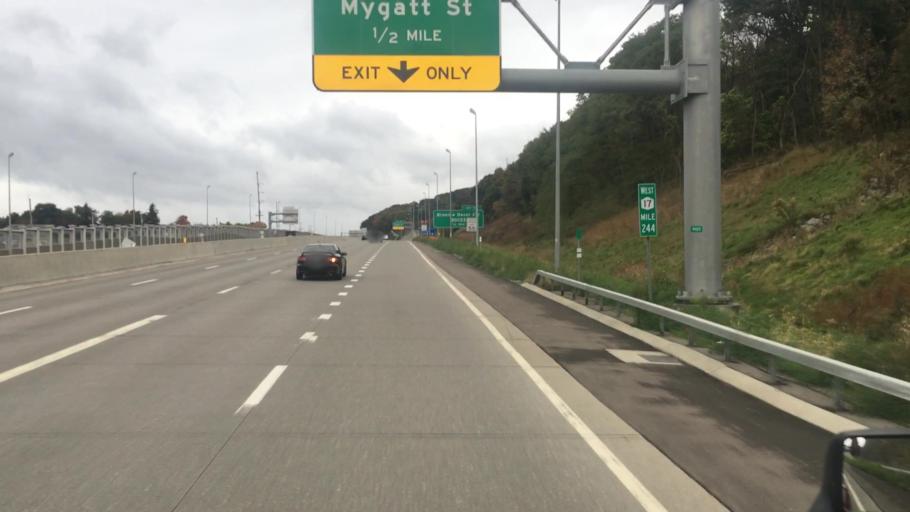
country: US
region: New York
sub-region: Broome County
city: Binghamton
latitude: 42.1119
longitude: -75.9154
